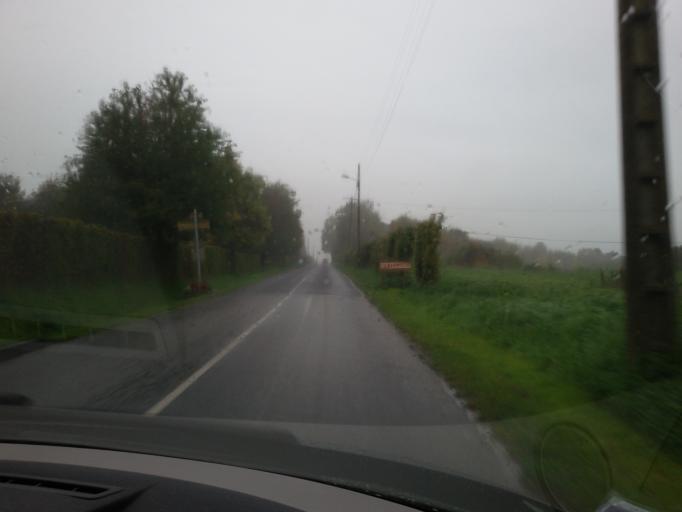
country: FR
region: Haute-Normandie
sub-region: Departement de la Seine-Maritime
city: La Cerlangue
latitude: 49.4221
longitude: 0.3907
